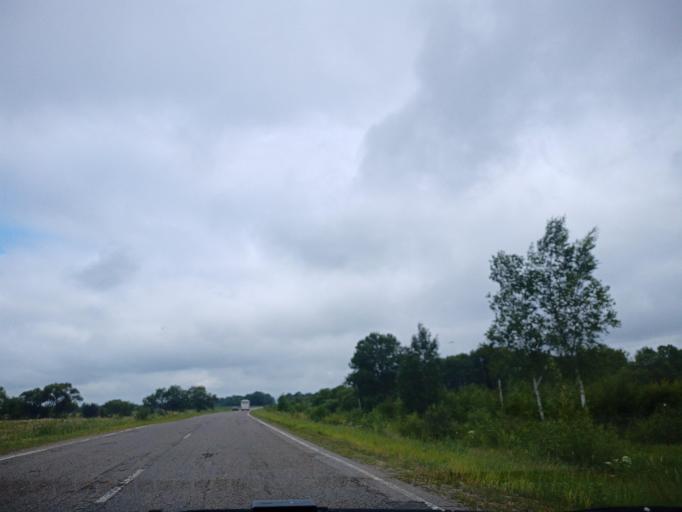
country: RU
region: Primorskiy
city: Novopokrovka
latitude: 45.9715
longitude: 134.2264
